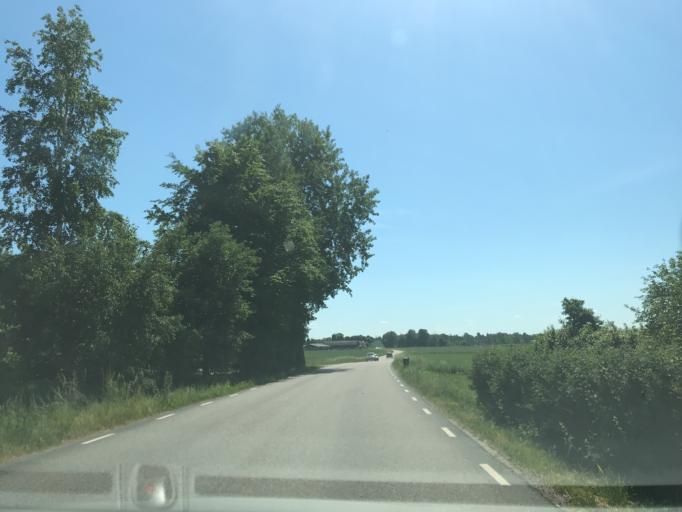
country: SE
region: Vaestra Goetaland
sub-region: Gotene Kommun
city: Kallby
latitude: 58.5213
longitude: 13.3219
